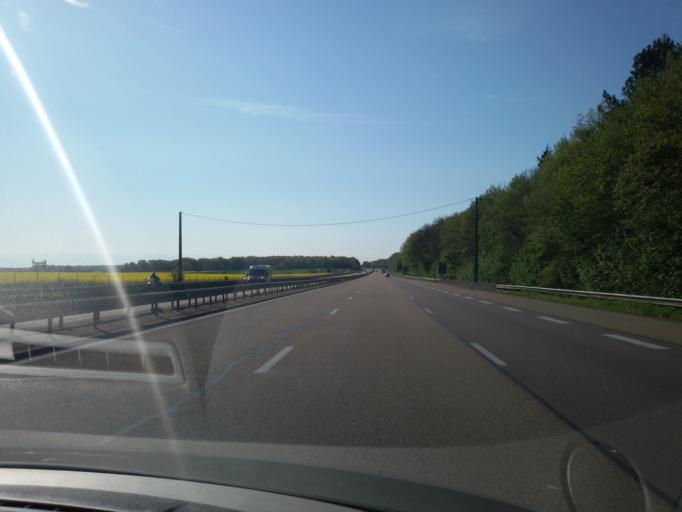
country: FR
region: Centre
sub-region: Departement du Loiret
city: Courtenay
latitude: 48.0137
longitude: 3.1475
